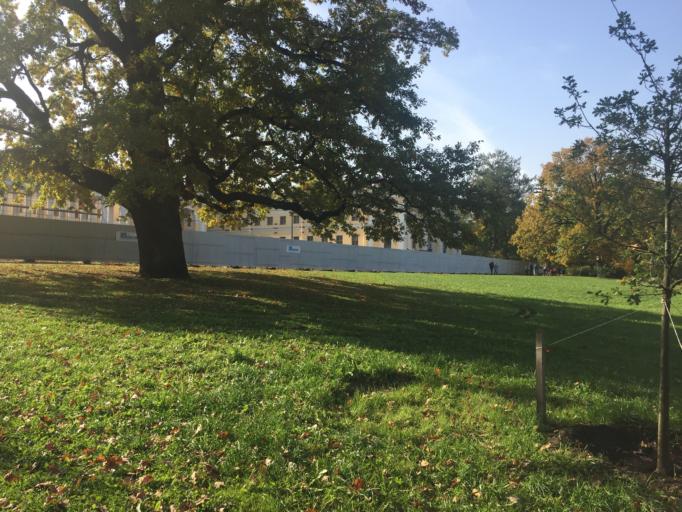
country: RU
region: St.-Petersburg
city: Pushkin
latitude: 59.7217
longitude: 30.3945
